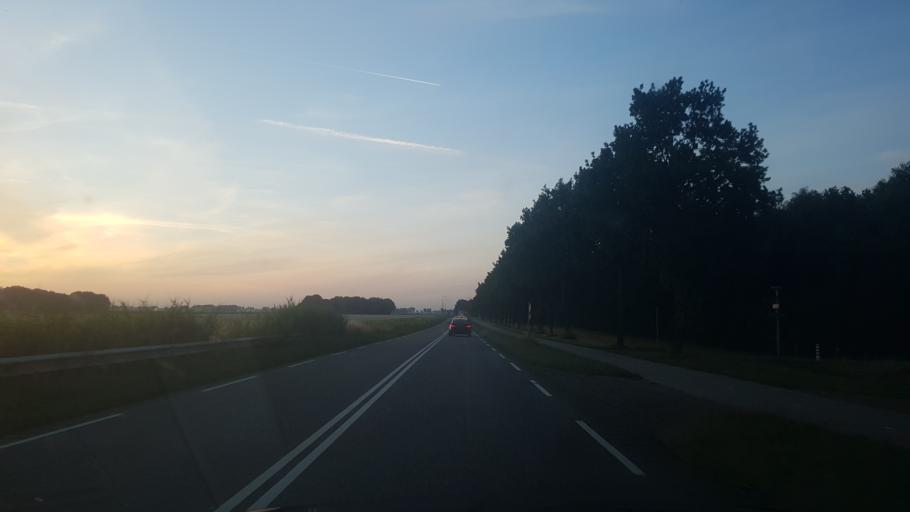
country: NL
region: Flevoland
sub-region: Gemeente Noordoostpolder
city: Emmeloord
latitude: 52.7166
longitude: 5.7199
